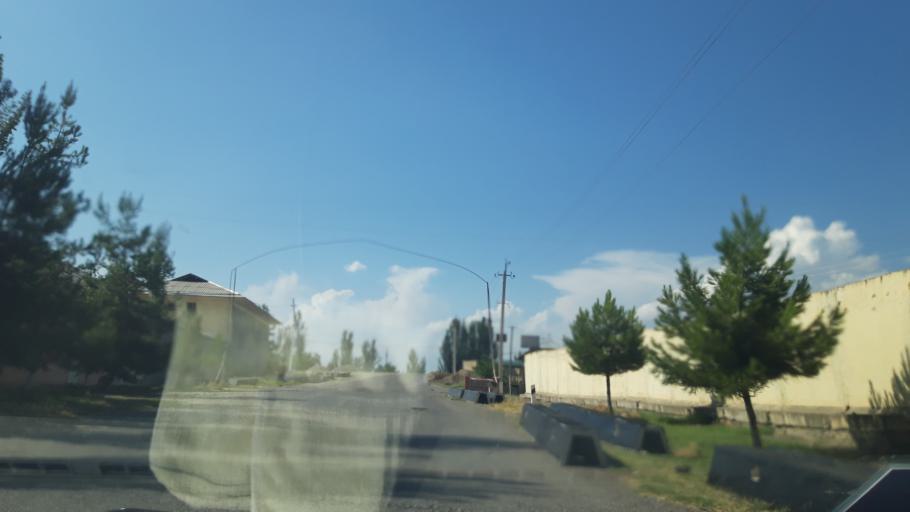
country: UZ
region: Namangan
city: Yangiqo`rg`on
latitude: 41.1993
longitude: 71.7037
